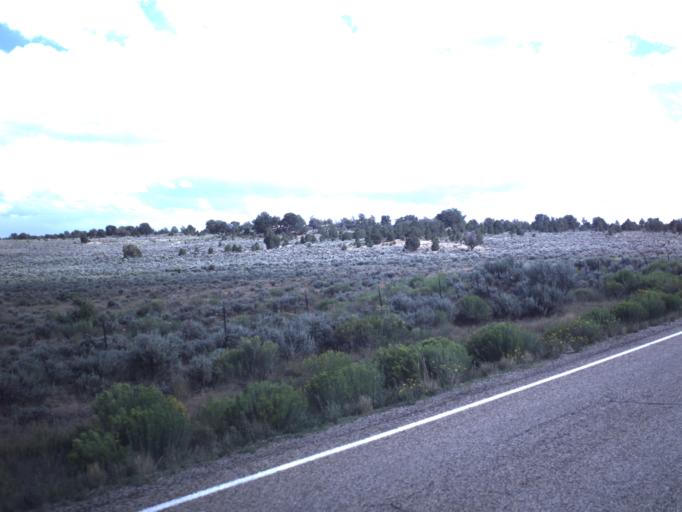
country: US
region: Utah
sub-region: Duchesne County
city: Duchesne
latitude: 40.2495
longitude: -110.7111
